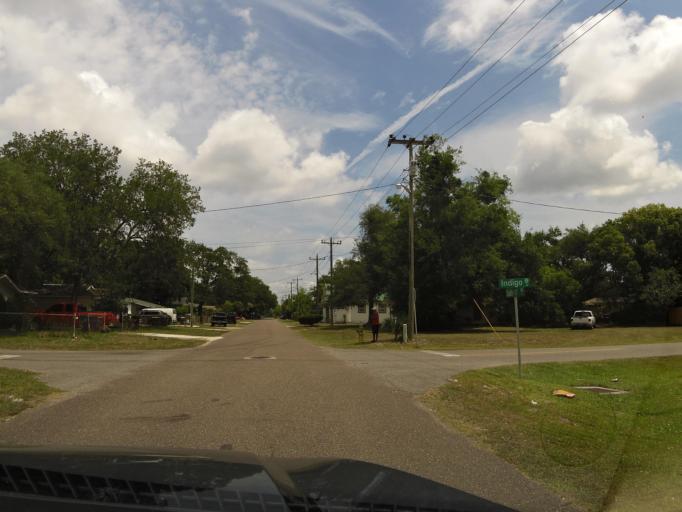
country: US
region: Florida
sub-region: Nassau County
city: Fernandina Beach
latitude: 30.6590
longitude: -81.4589
